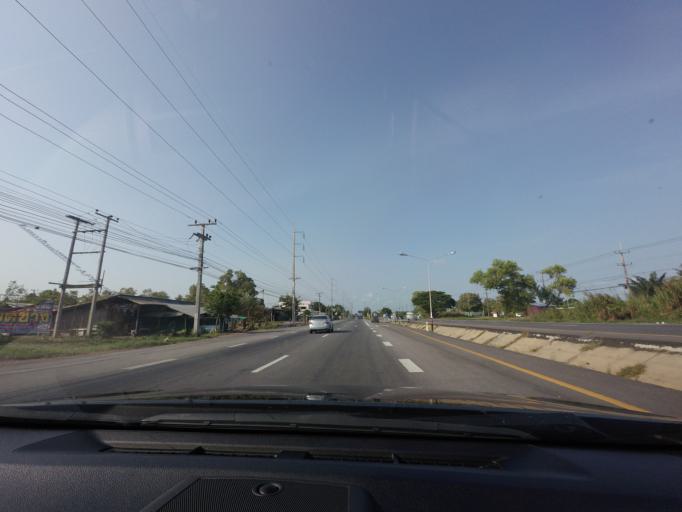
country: TH
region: Prachuap Khiri Khan
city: Kui Buri
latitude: 11.9574
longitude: 99.8301
